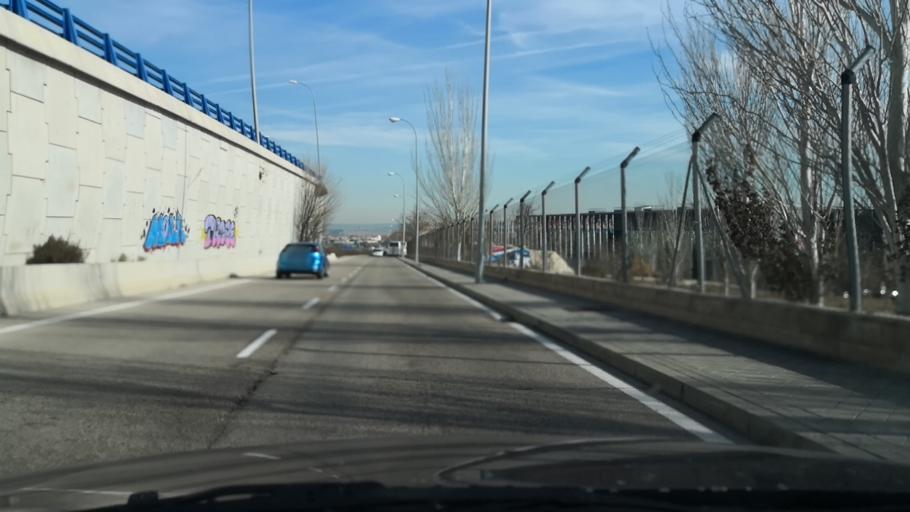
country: ES
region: Madrid
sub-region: Provincia de Madrid
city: Hortaleza
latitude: 40.4719
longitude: -3.6208
